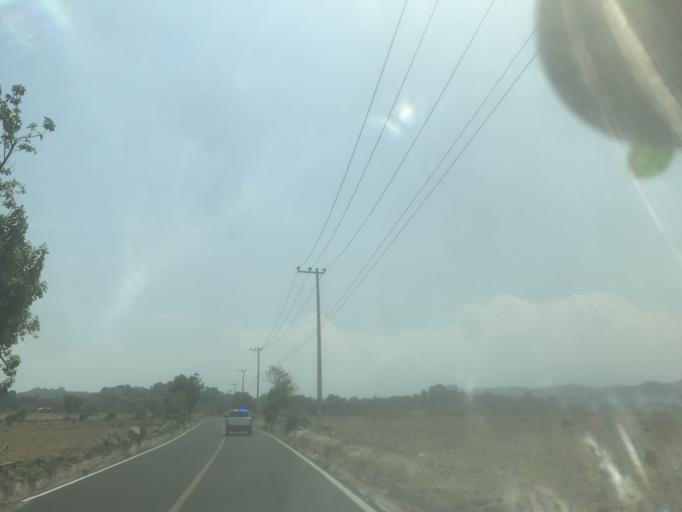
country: MX
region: Morelos
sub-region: Yecapixtla
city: Achichipico
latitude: 18.9578
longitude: -98.8295
